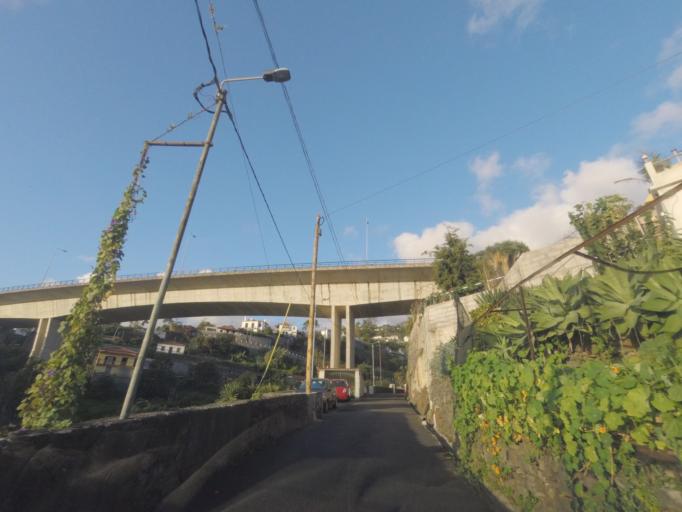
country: PT
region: Madeira
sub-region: Funchal
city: Nossa Senhora do Monte
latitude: 32.6547
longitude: -16.8821
